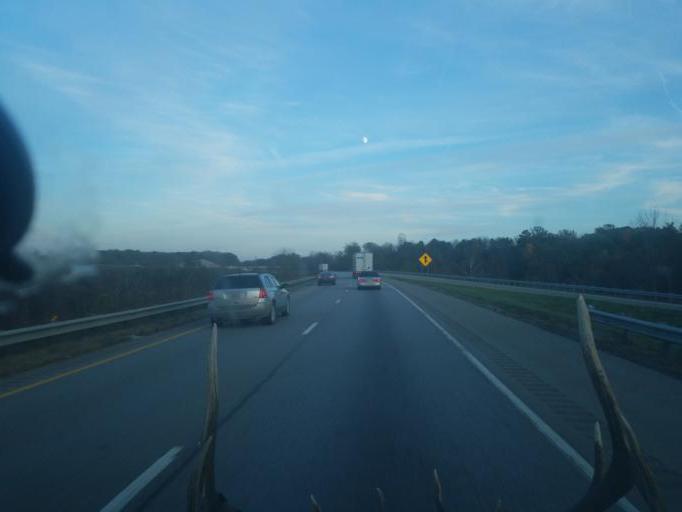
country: US
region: Ohio
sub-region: Muskingum County
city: New Concord
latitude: 39.9729
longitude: -81.8316
